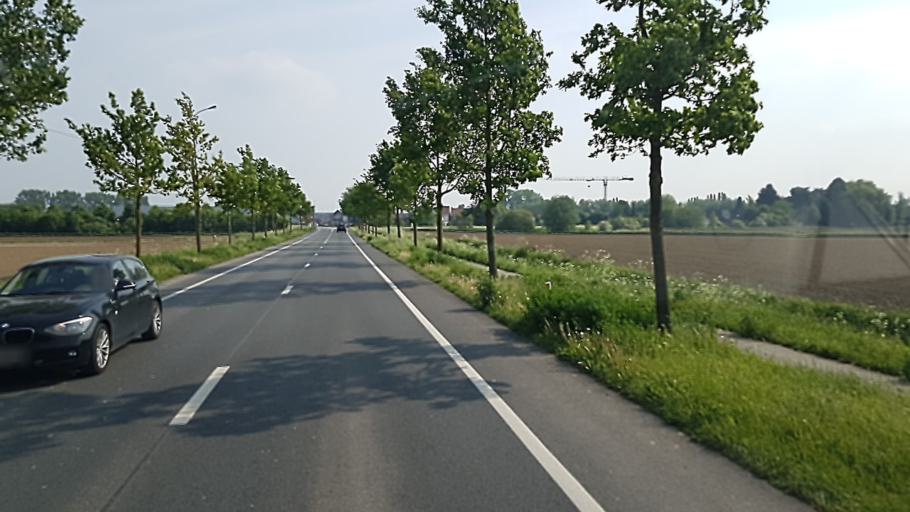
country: BE
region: Wallonia
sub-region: Province du Hainaut
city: Pecq
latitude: 50.7328
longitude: 3.3291
